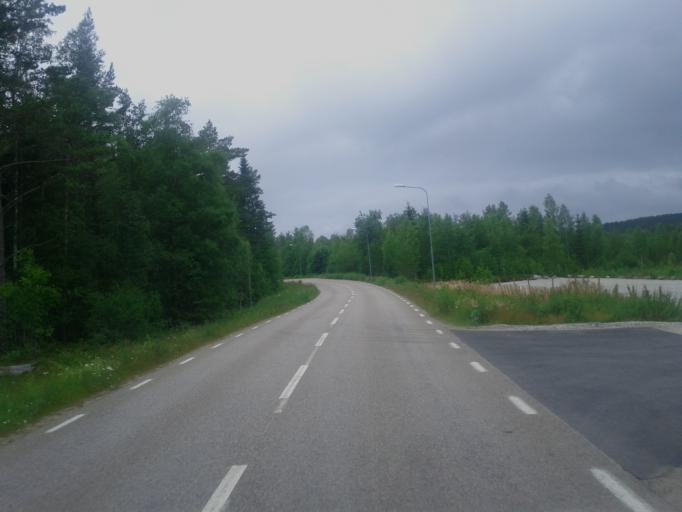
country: SE
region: Gaevleborg
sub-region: Nordanstigs Kommun
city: Bergsjoe
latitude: 61.9610
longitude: 17.3223
